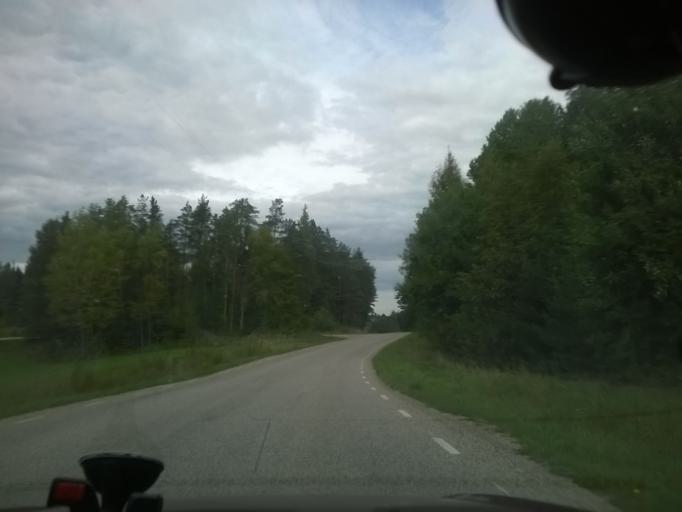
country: EE
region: Vorumaa
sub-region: Voru linn
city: Voru
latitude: 57.7742
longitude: 27.0257
